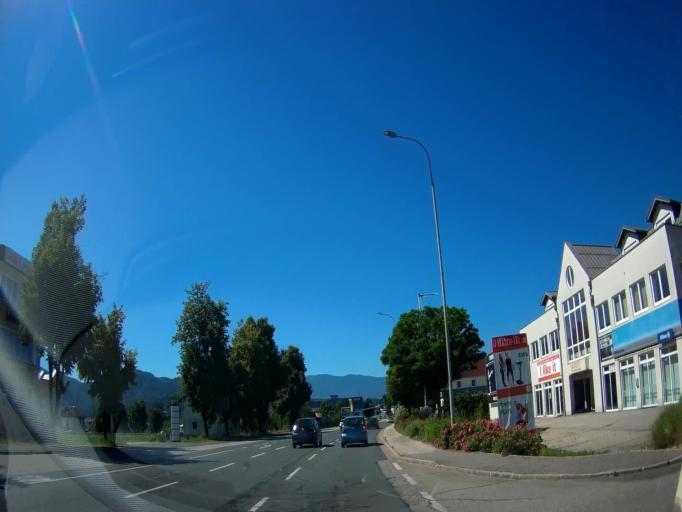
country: AT
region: Carinthia
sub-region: Klagenfurt am Woerthersee
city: Klagenfurt am Woerthersee
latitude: 46.6011
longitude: 14.2967
